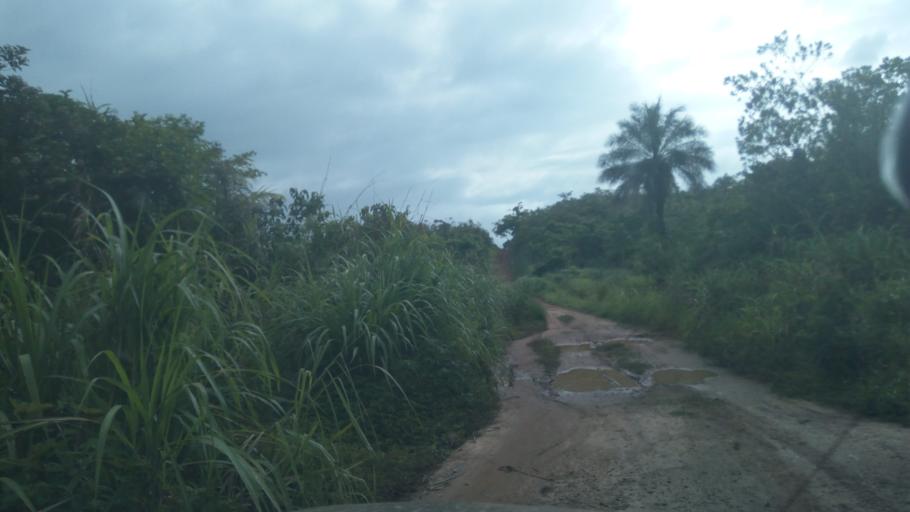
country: SL
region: Southern Province
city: Bomi
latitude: 7.2402
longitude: -11.5317
